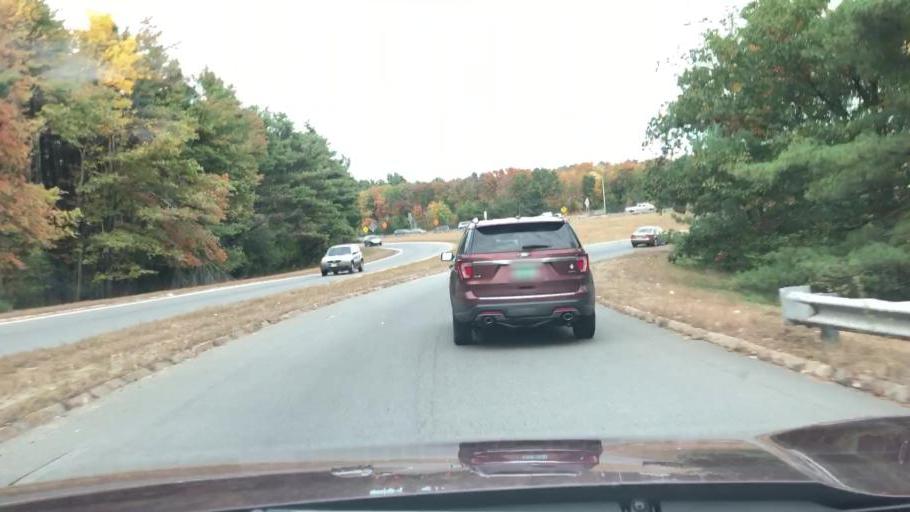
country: US
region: Massachusetts
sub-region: Essex County
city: Lawrence
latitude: 42.6651
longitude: -71.1968
